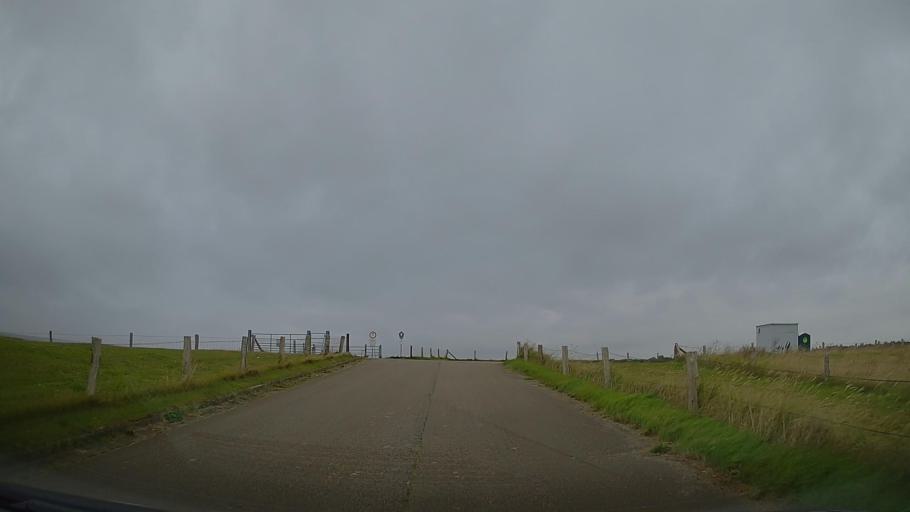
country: DE
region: Schleswig-Holstein
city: Busenwurth
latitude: 54.0686
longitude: 8.9818
